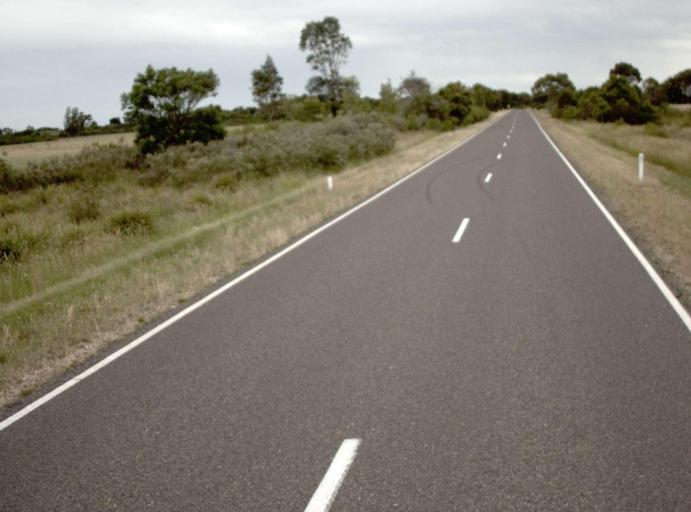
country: AU
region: Victoria
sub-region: East Gippsland
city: Bairnsdale
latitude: -37.9873
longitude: 147.3992
